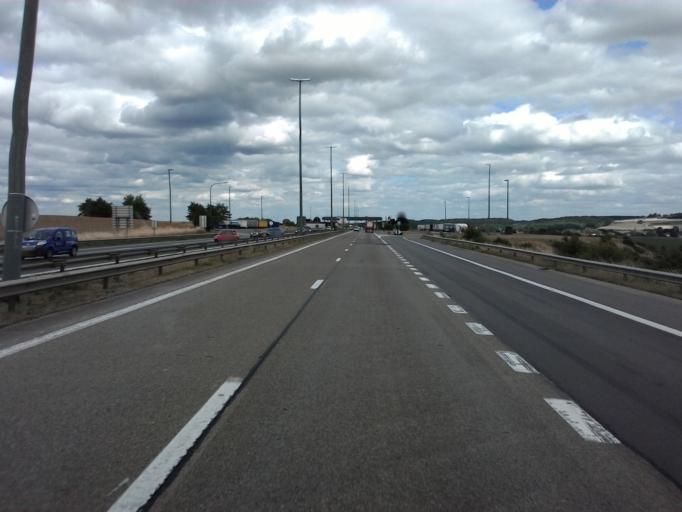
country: LU
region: Luxembourg
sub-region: Canton de Capellen
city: Steinfort
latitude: 49.6393
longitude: 5.8980
